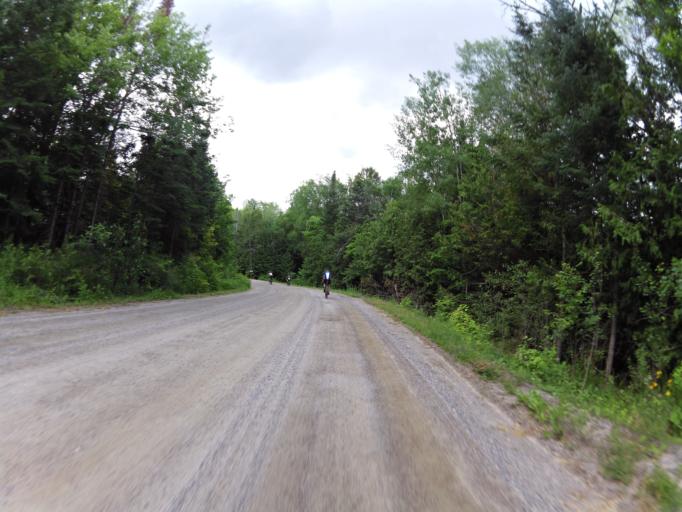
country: CA
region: Ontario
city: Renfrew
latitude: 45.1274
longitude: -76.6336
